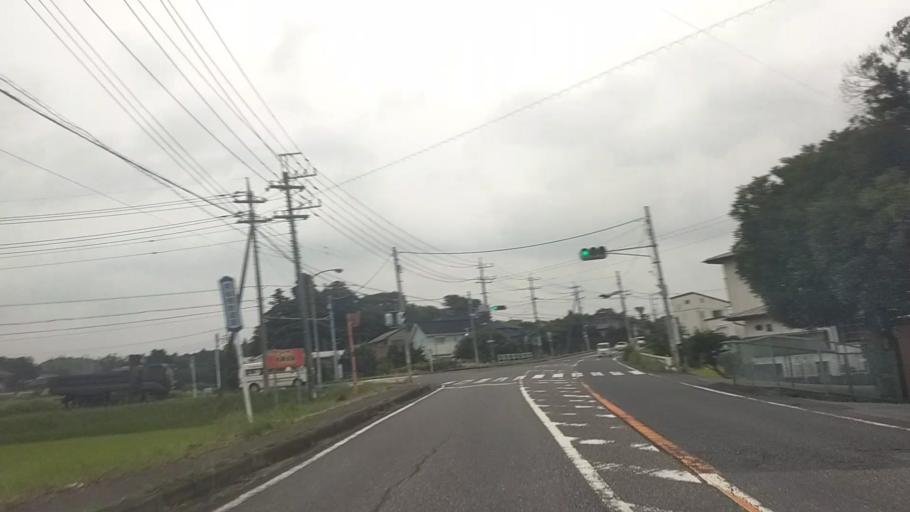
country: JP
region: Chiba
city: Kisarazu
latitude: 35.3888
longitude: 140.0477
